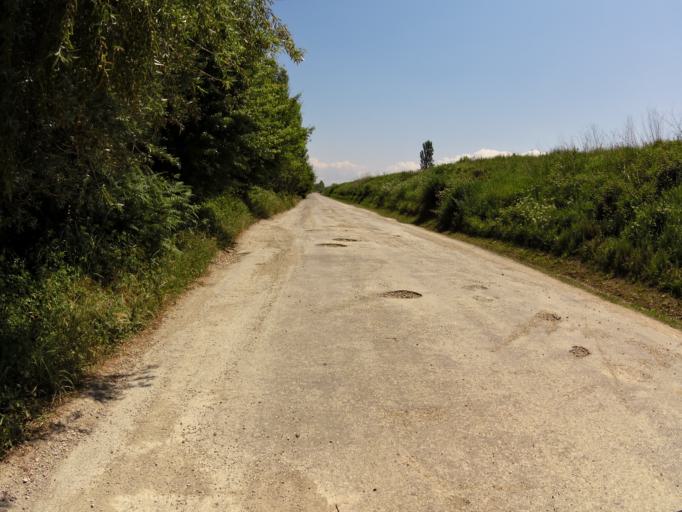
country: PT
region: Coimbra
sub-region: Montemor-O-Velho
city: Montemor-o-Velho
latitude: 40.1490
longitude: -8.7273
